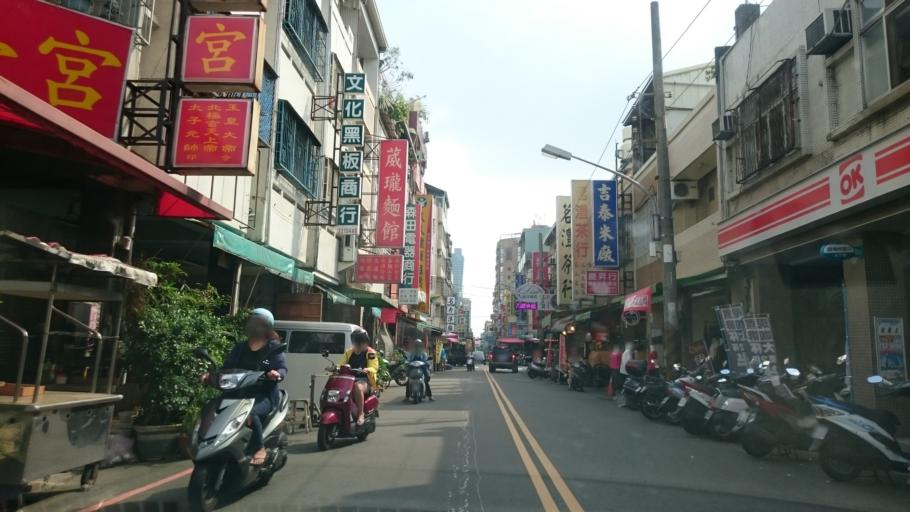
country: TW
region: Taiwan
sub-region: Taichung City
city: Taichung
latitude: 24.1486
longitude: 120.6588
